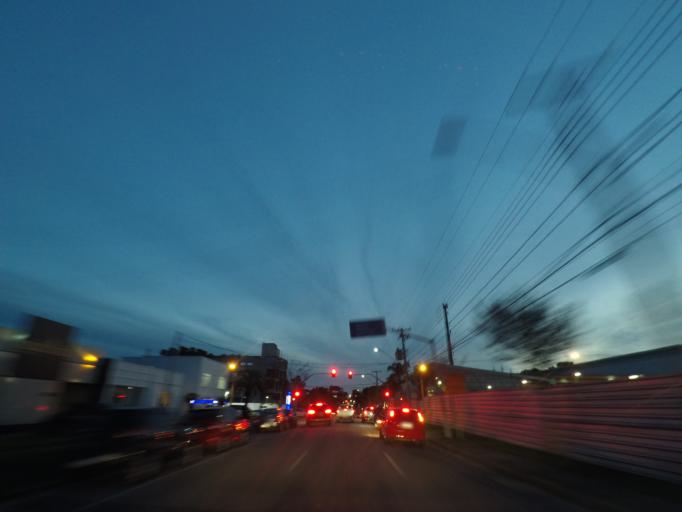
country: BR
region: Parana
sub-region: Curitiba
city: Curitiba
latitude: -25.4386
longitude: -49.2940
